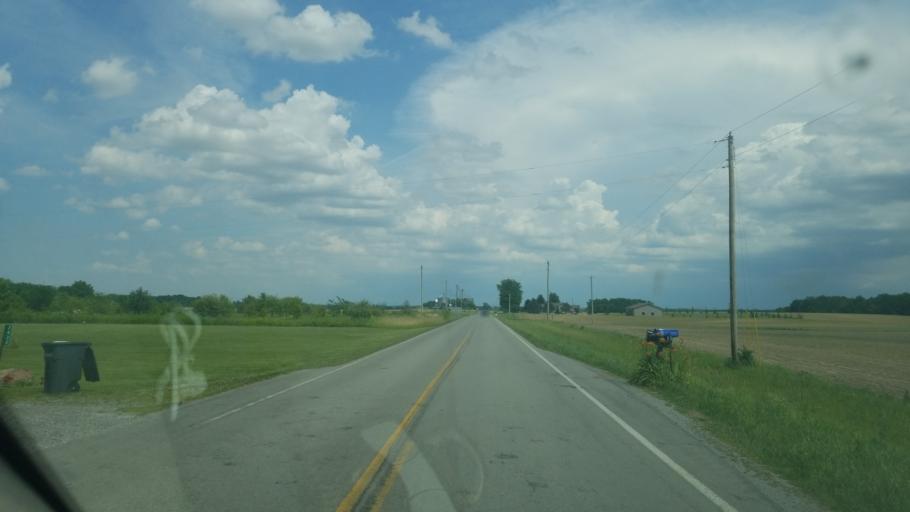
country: US
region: Ohio
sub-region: Hardin County
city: Ada
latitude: 40.6160
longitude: -83.8340
